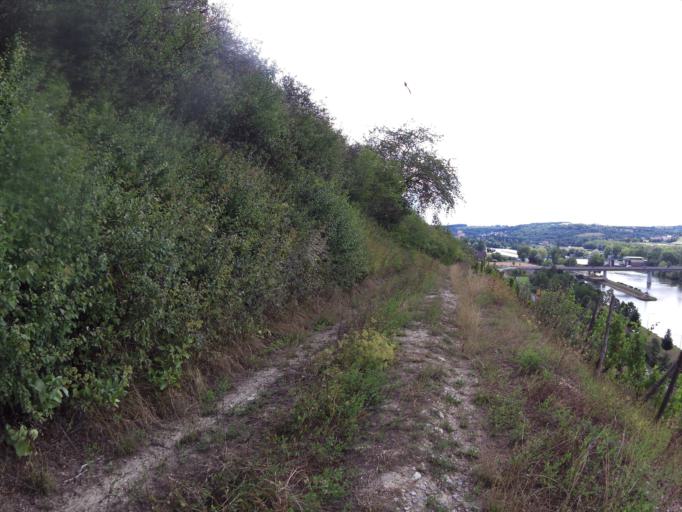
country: DE
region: Bavaria
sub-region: Regierungsbezirk Unterfranken
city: Sommerhausen
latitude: 49.6836
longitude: 10.0343
